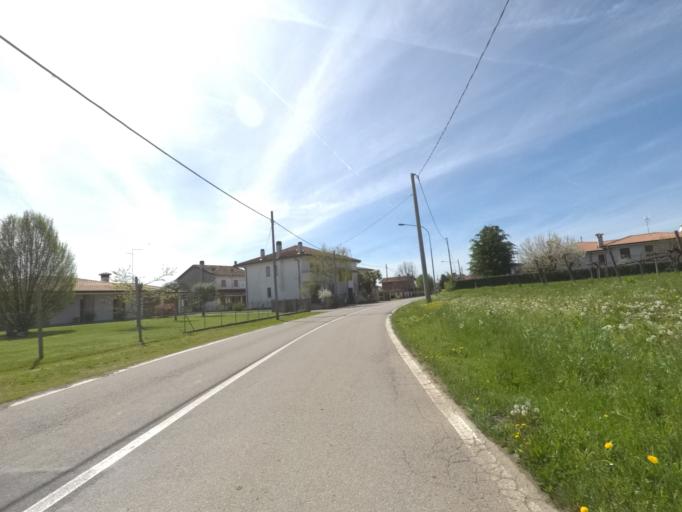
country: IT
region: Friuli Venezia Giulia
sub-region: Provincia di Pordenone
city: Casarsa della Delizia
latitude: 45.9443
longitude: 12.8520
